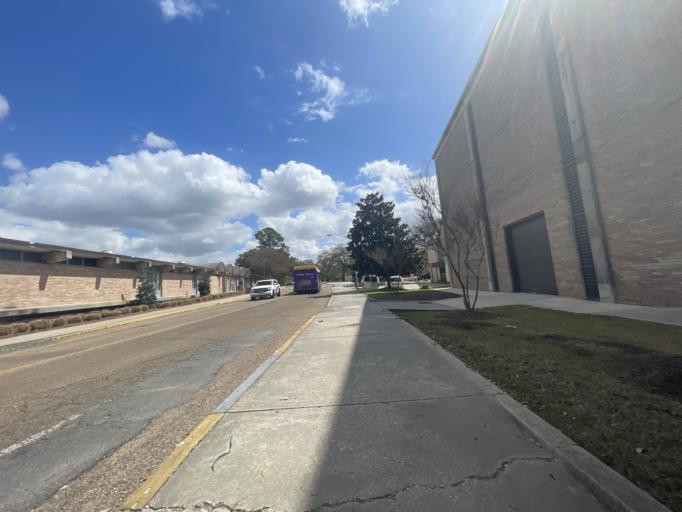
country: US
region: Louisiana
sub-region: East Baton Rouge Parish
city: Baton Rouge
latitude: 30.4096
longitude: -91.1807
